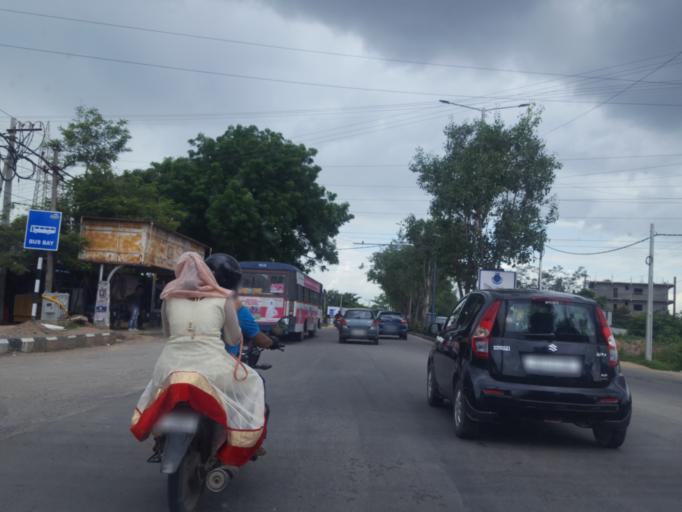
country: IN
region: Telangana
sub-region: Medak
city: Serilingampalle
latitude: 17.4681
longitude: 78.3312
